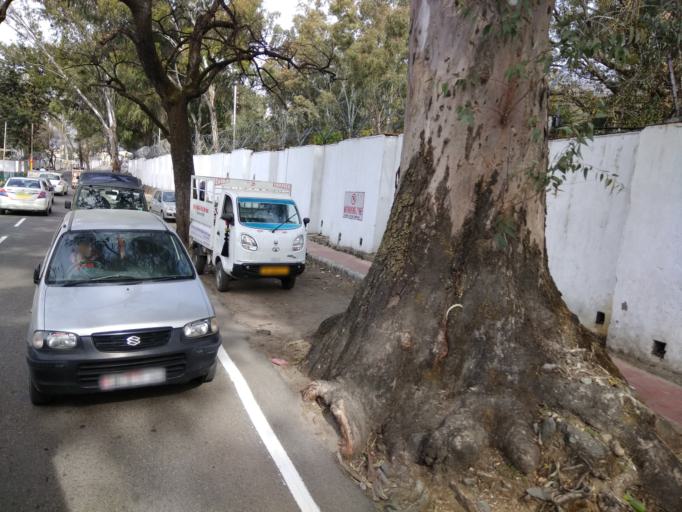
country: IN
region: Himachal Pradesh
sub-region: Kangra
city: Dharmsala
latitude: 32.1792
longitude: 76.3784
